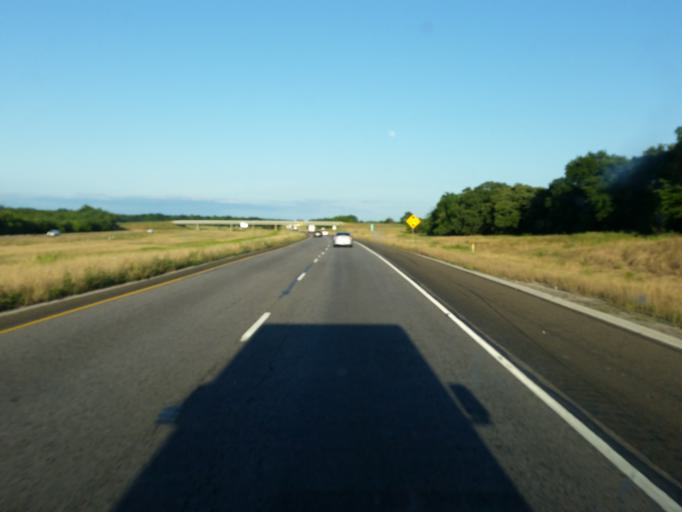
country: US
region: Texas
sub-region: Kaufman County
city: Terrell
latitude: 32.6784
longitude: -96.1866
